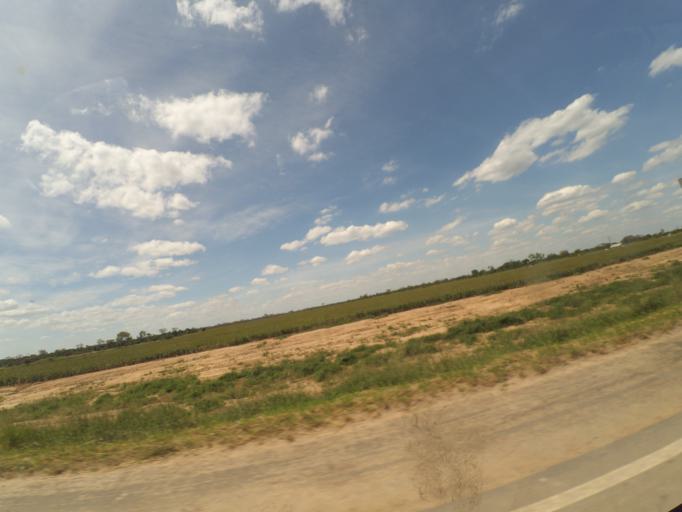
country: BO
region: Santa Cruz
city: Pailon
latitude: -17.5889
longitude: -61.9558
